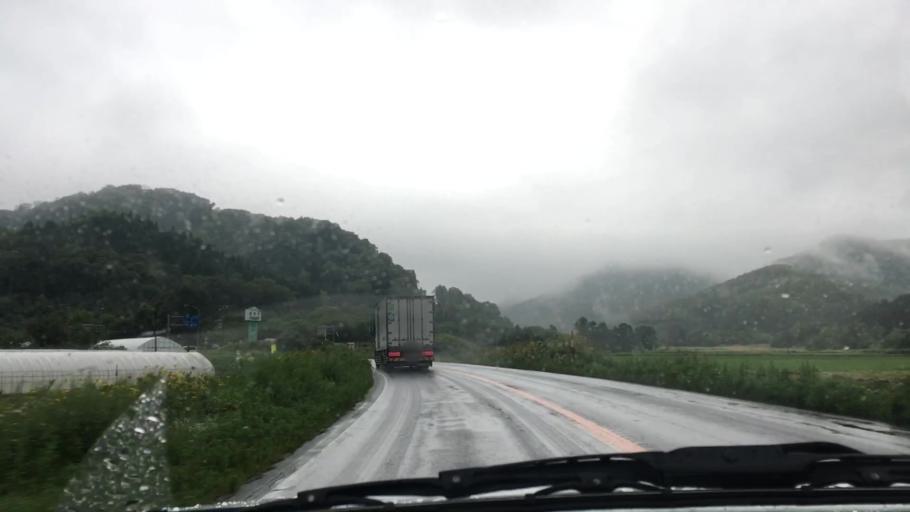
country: JP
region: Hokkaido
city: Niseko Town
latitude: 42.6010
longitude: 140.5866
